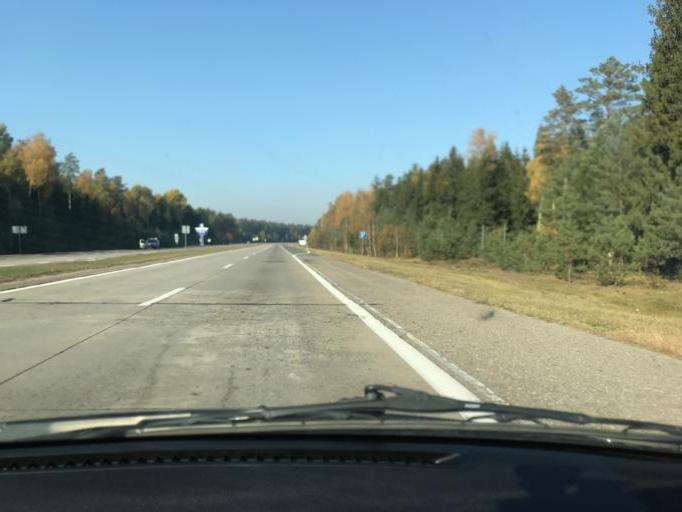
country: BY
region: Minsk
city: Uzda
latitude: 53.3768
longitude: 27.4971
